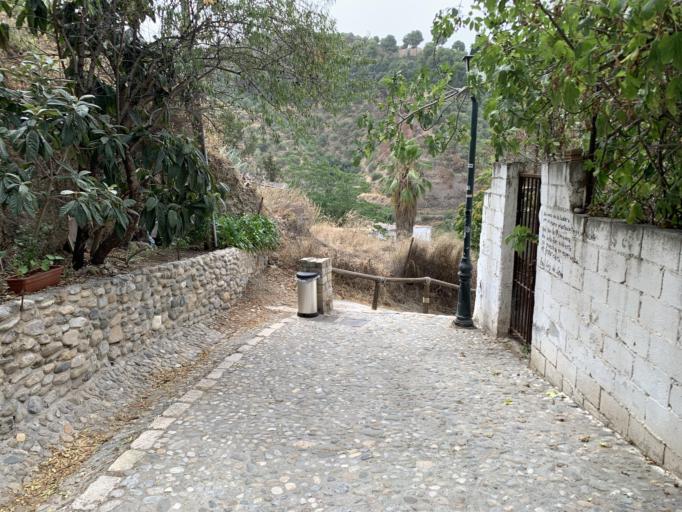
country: ES
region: Andalusia
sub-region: Provincia de Granada
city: Granada
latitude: 37.1826
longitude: -3.5842
